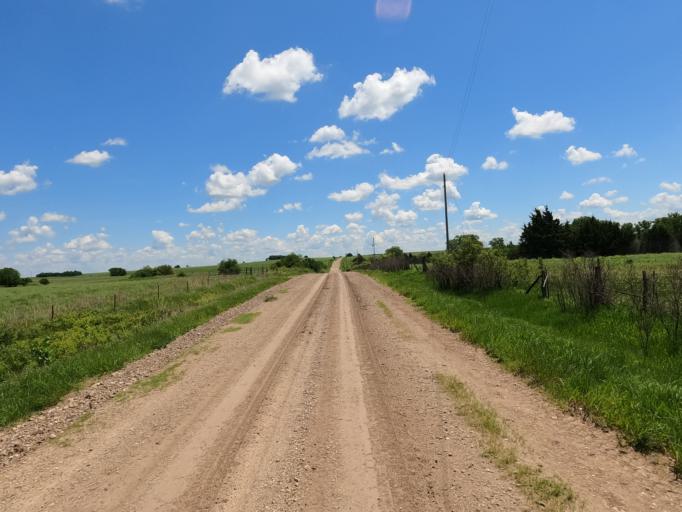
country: US
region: Kansas
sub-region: Chase County
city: Cottonwood Falls
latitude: 38.2165
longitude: -96.7723
